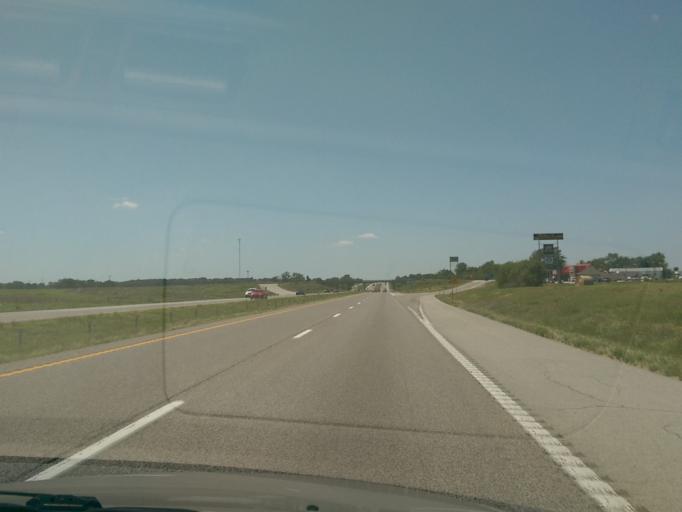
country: US
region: Missouri
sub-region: Saline County
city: Marshall
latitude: 38.9529
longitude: -93.0841
